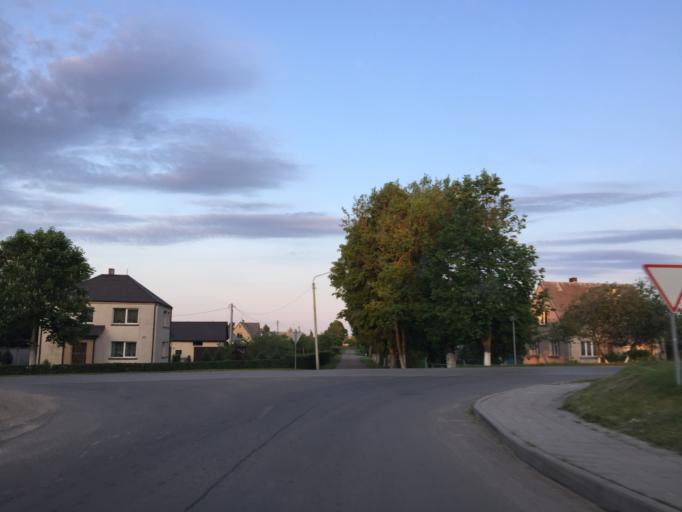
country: LT
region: Siauliu apskritis
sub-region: Siauliai
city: Siauliai
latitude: 55.9841
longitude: 23.1398
